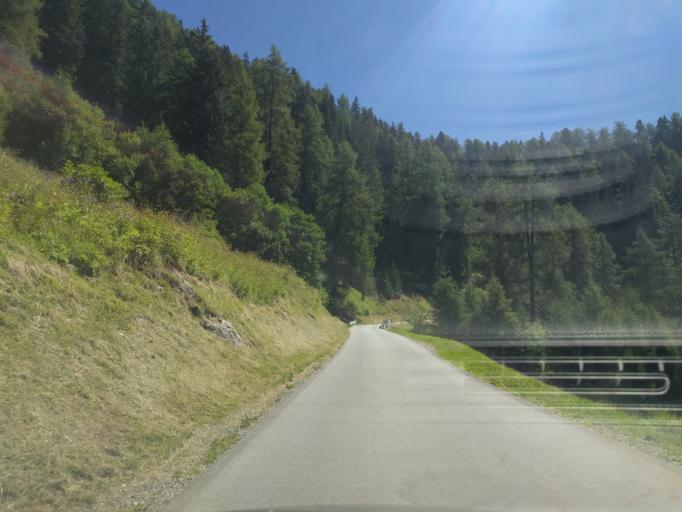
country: IT
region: Trentino-Alto Adige
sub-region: Bolzano
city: Tubre
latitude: 46.6112
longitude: 10.3907
